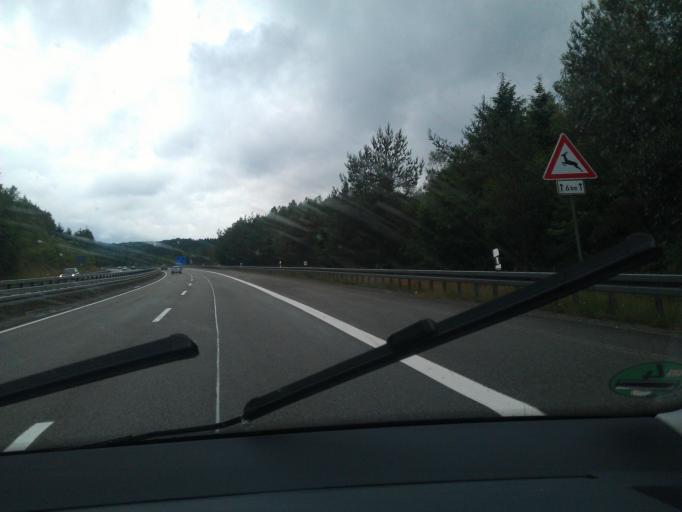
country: DE
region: Rheinland-Pfalz
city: Ellweiler
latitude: 49.6019
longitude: 7.1586
